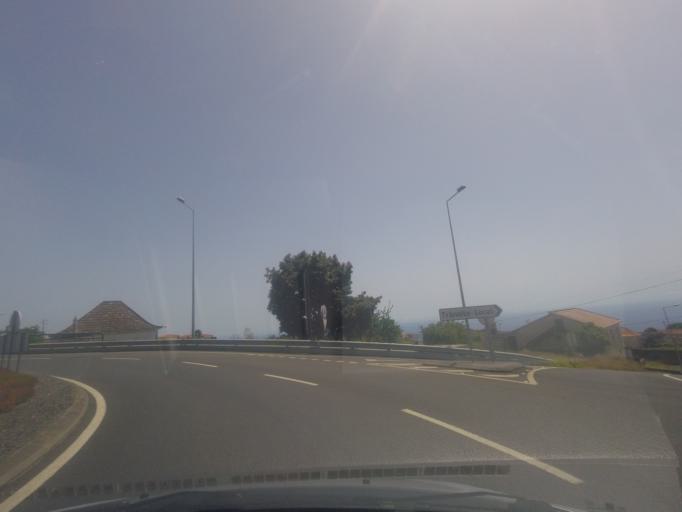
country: PT
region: Madeira
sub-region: Calheta
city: Faja da Ovelha
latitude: 32.7693
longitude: -17.2165
